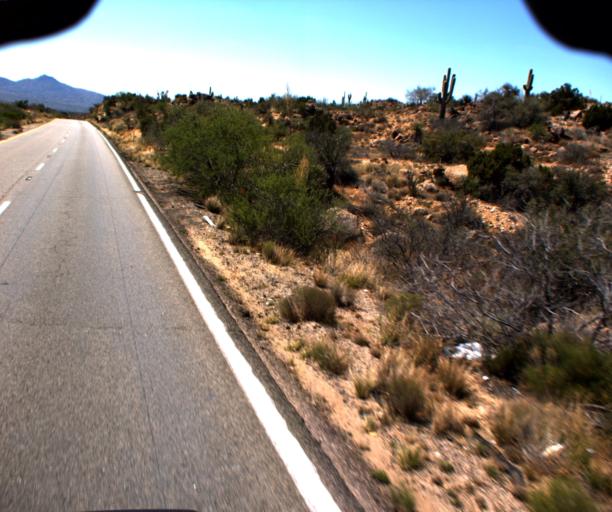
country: US
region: Arizona
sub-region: Yavapai County
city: Bagdad
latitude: 34.4829
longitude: -113.3495
